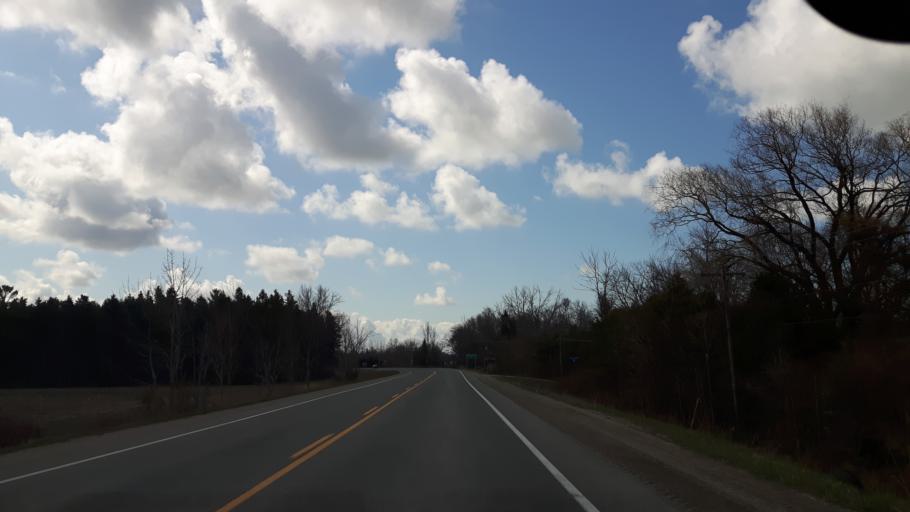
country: CA
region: Ontario
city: Bluewater
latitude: 43.5780
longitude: -81.7056
